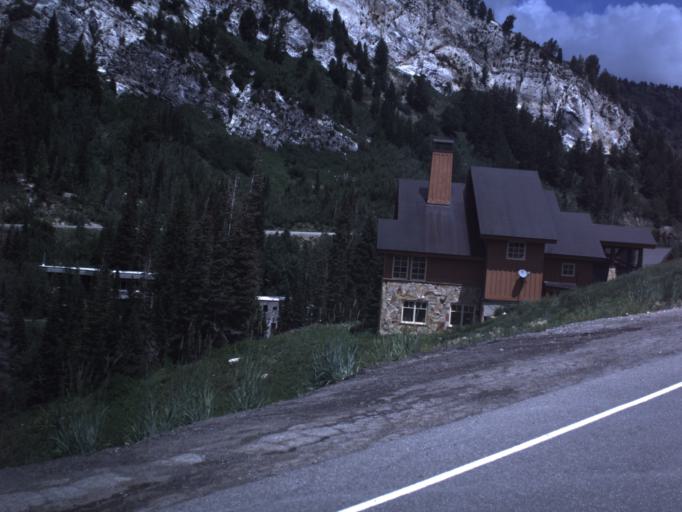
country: US
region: Utah
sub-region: Summit County
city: Snyderville
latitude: 40.5867
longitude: -111.6488
